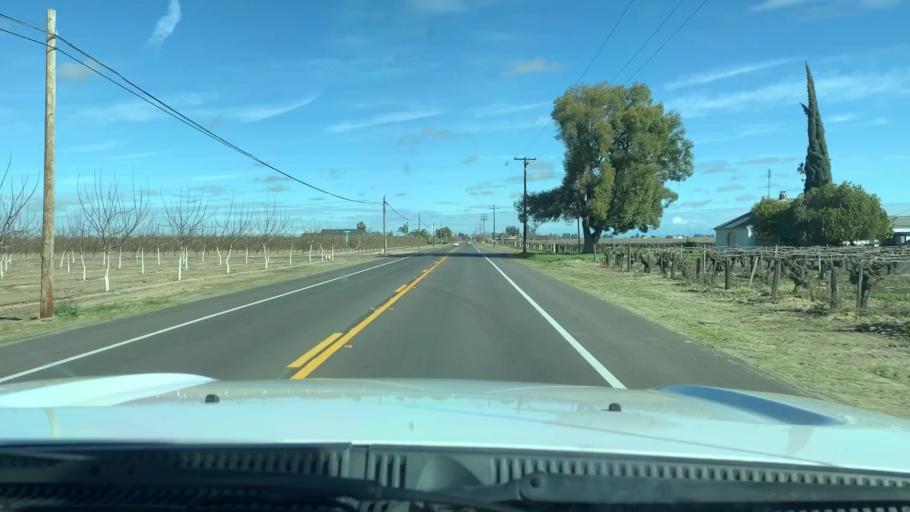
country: US
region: California
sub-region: Fresno County
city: Selma
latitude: 36.5356
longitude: -119.6828
